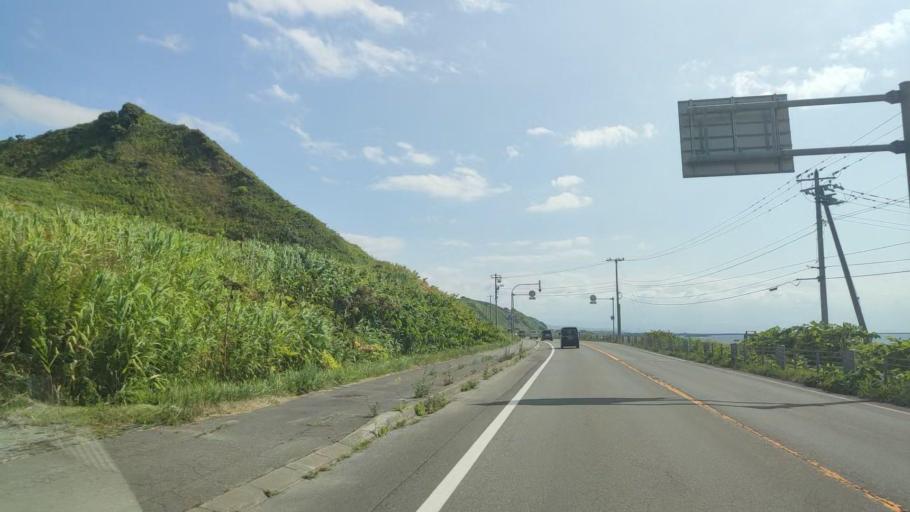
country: JP
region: Hokkaido
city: Rumoi
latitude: 43.9948
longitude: 141.6518
